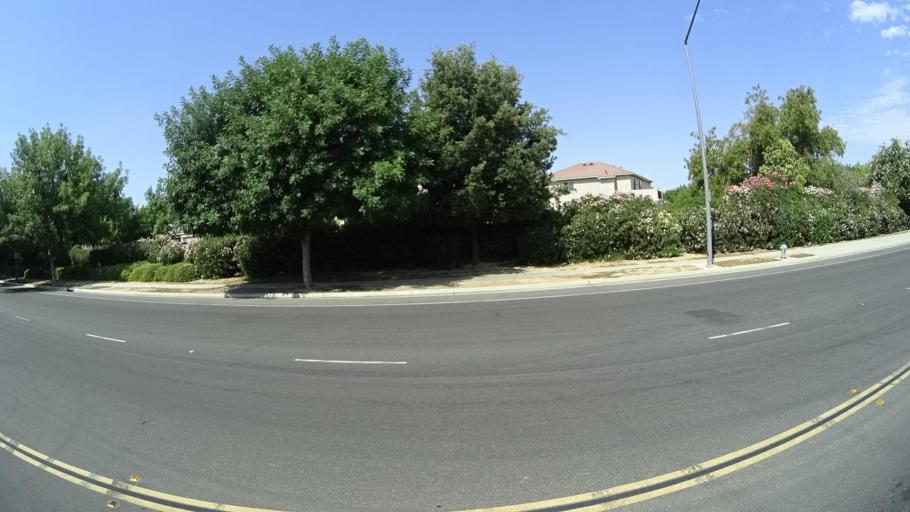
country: US
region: California
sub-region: Fresno County
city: Sunnyside
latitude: 36.7197
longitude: -119.6913
